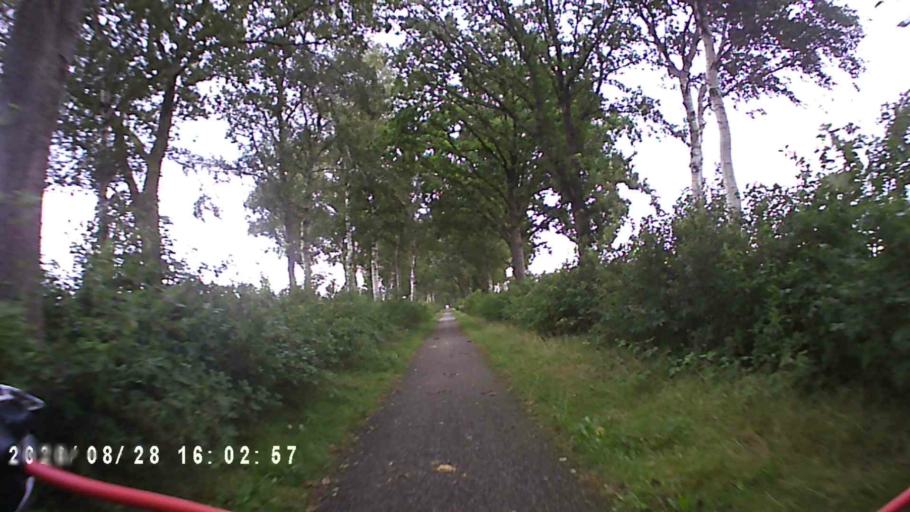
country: NL
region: Drenthe
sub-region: Gemeente Tynaarlo
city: Vries
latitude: 53.1088
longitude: 6.4991
